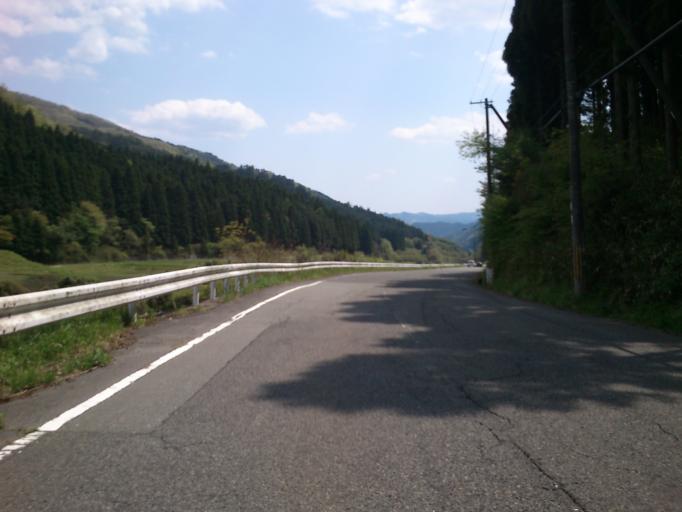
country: JP
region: Hyogo
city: Toyooka
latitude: 35.3860
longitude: 134.9399
